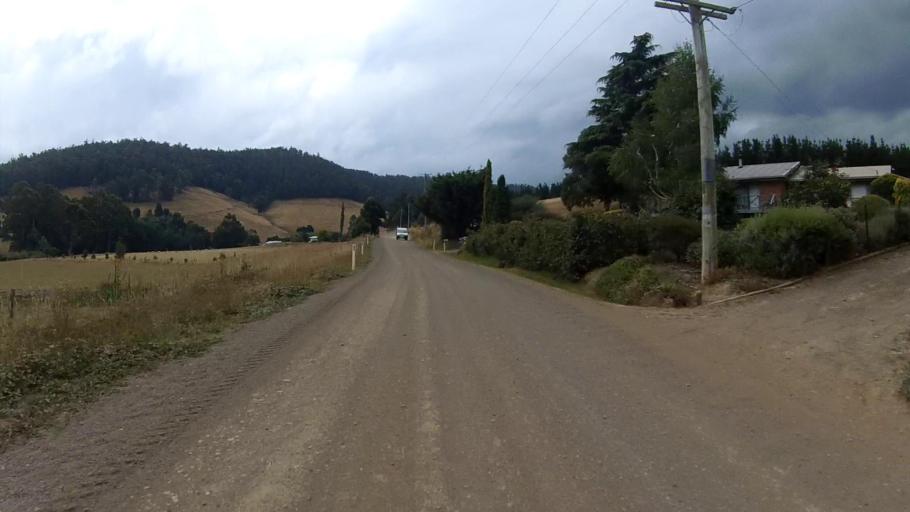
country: AU
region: Tasmania
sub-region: Huon Valley
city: Huonville
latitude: -42.9744
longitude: 147.0543
